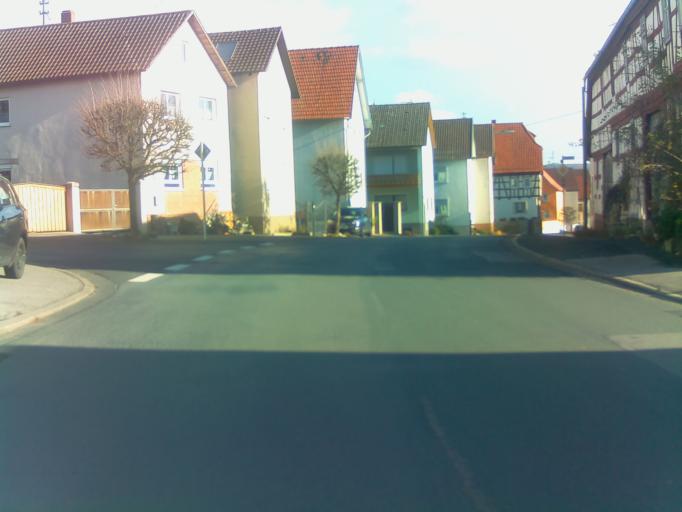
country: DE
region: Bavaria
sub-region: Regierungsbezirk Unterfranken
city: Herbstadt
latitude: 50.3109
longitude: 10.5243
